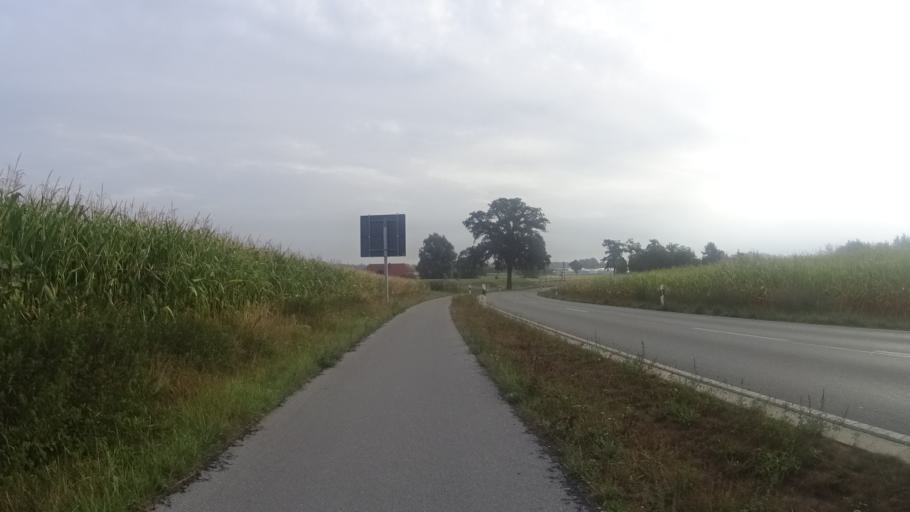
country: DE
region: North Rhine-Westphalia
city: Straelen
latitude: 51.5011
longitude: 6.2519
